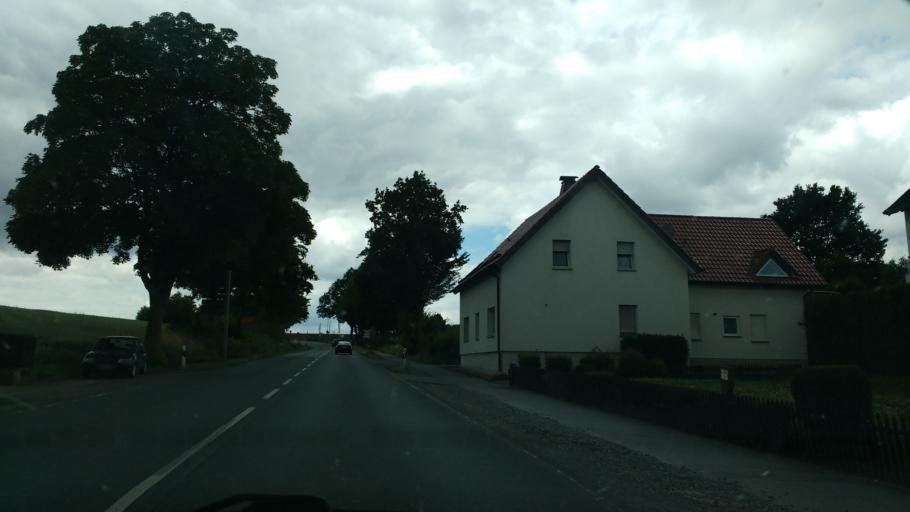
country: DE
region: North Rhine-Westphalia
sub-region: Regierungsbezirk Detmold
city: Bad Meinberg
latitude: 51.8948
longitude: 8.9720
